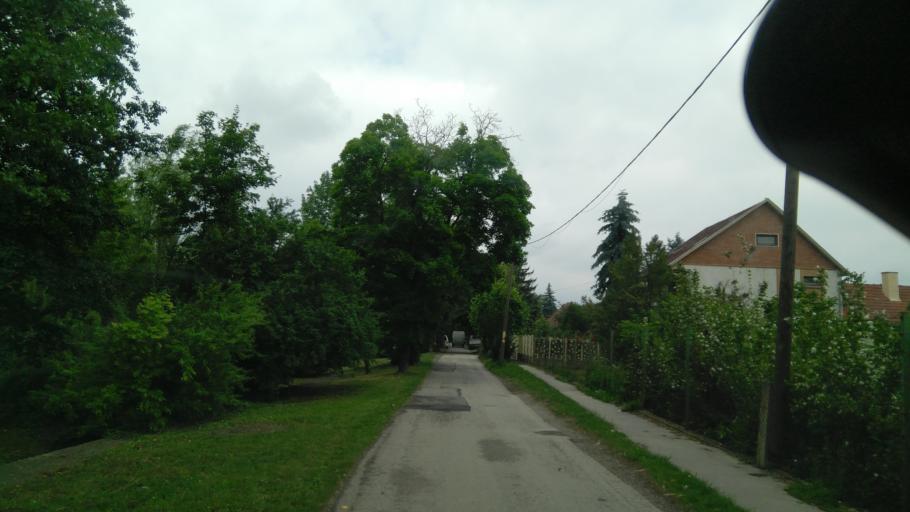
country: HU
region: Bekes
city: Bekescsaba
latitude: 46.6872
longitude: 21.1001
